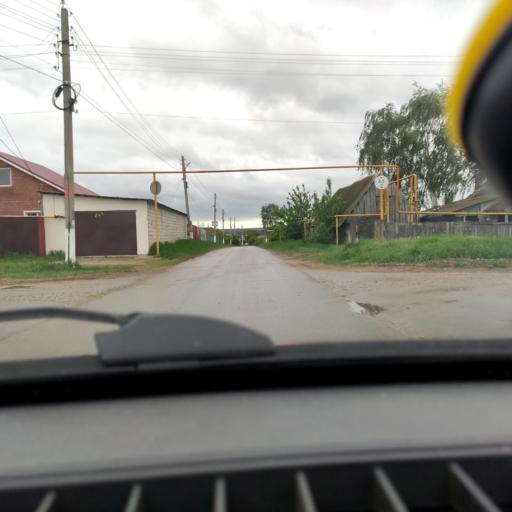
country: RU
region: Samara
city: Zhigulevsk
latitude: 53.5546
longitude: 49.5336
